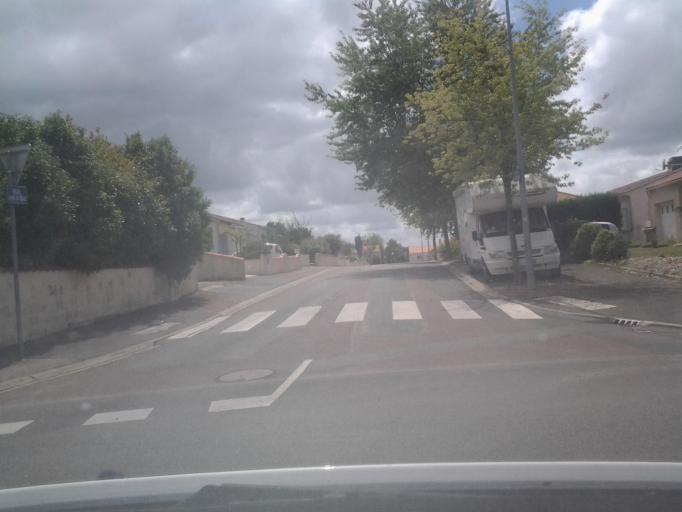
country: FR
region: Pays de la Loire
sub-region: Departement de la Vendee
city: La Roche-sur-Yon
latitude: 46.6566
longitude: -1.4531
